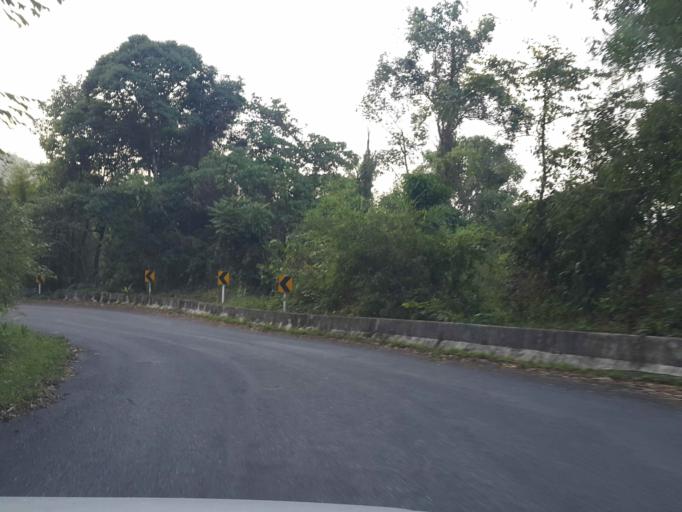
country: TH
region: Chiang Mai
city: Mae On
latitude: 19.0011
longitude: 99.3322
